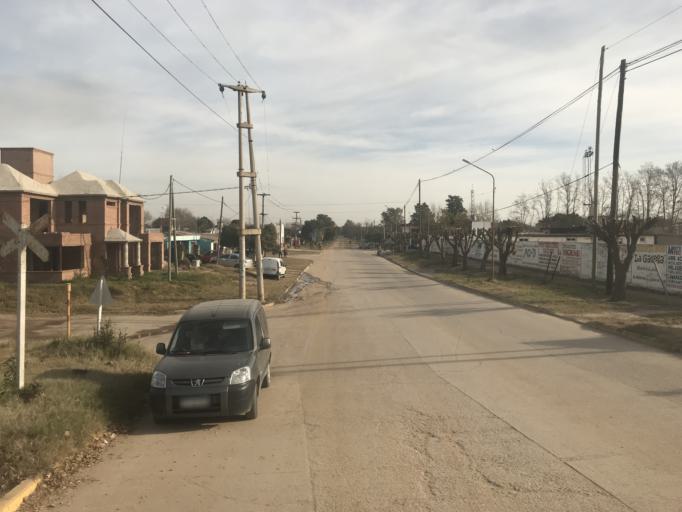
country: AR
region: Cordoba
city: Pilar
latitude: -31.6856
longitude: -63.8827
